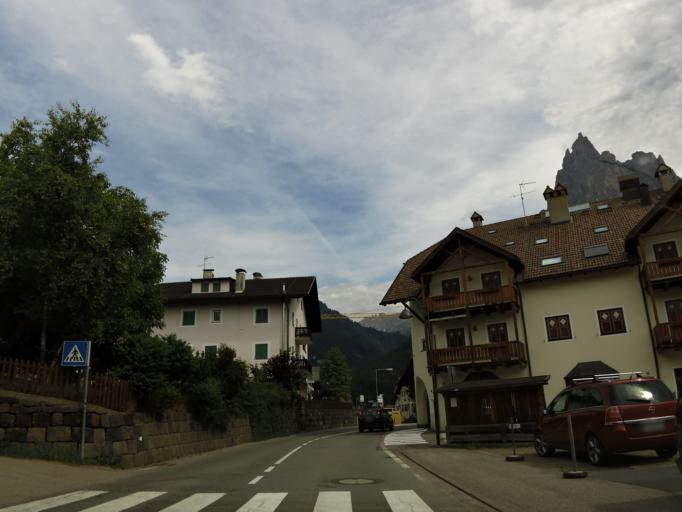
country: IT
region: Trentino-Alto Adige
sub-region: Bolzano
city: Siusi
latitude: 46.5462
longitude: 11.5603
